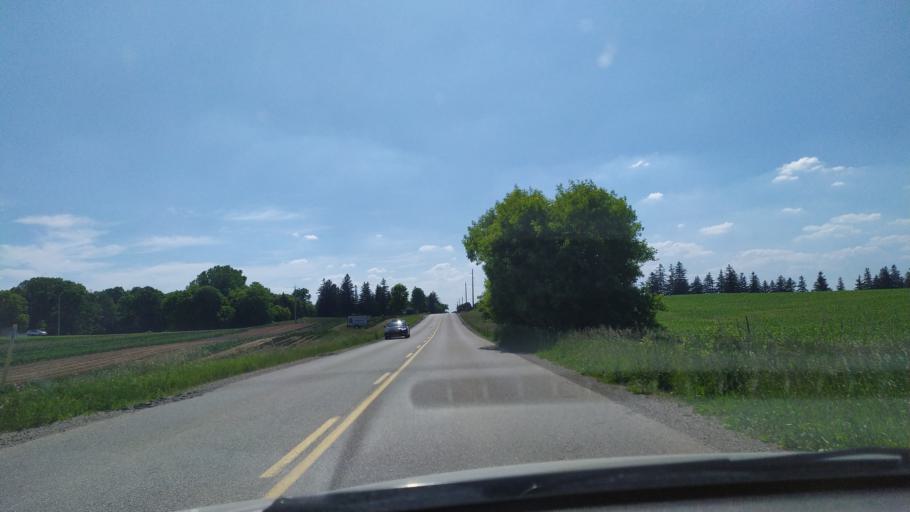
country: CA
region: Ontario
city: Kitchener
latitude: 43.3745
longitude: -80.5364
